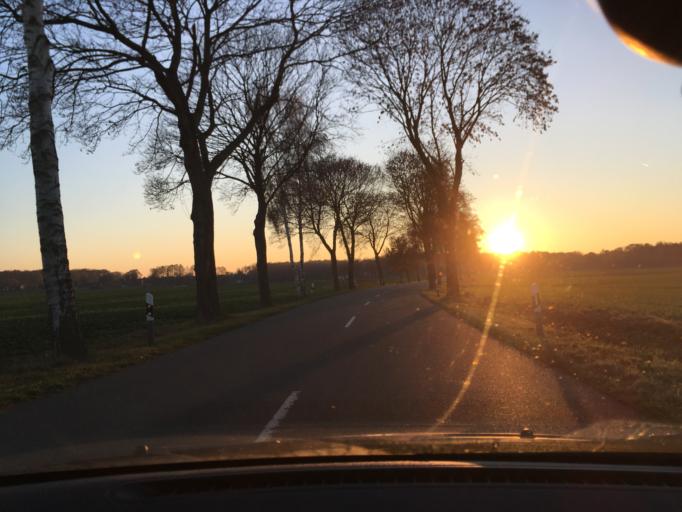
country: DE
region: Lower Saxony
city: Ebstorf
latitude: 53.0419
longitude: 10.4304
